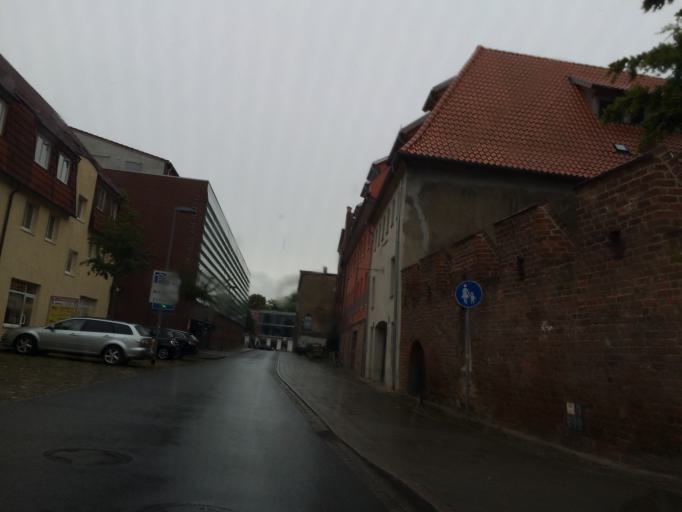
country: DE
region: Mecklenburg-Vorpommern
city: Stralsund
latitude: 54.3174
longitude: 13.0926
